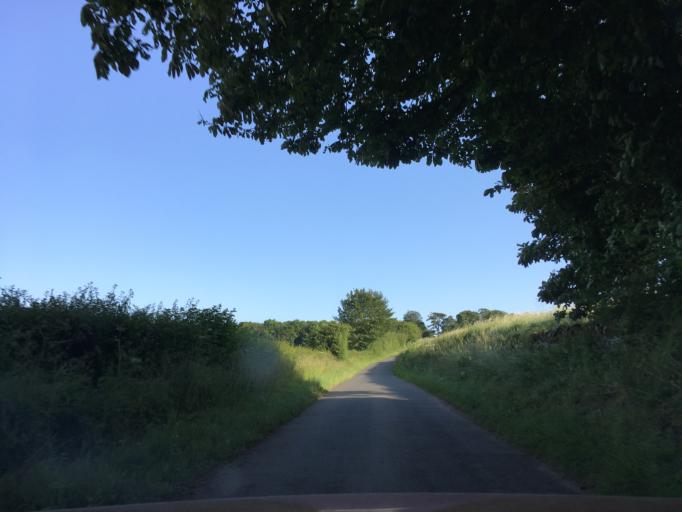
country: GB
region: England
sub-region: Gloucestershire
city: Lechlade
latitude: 51.7597
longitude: -1.7230
